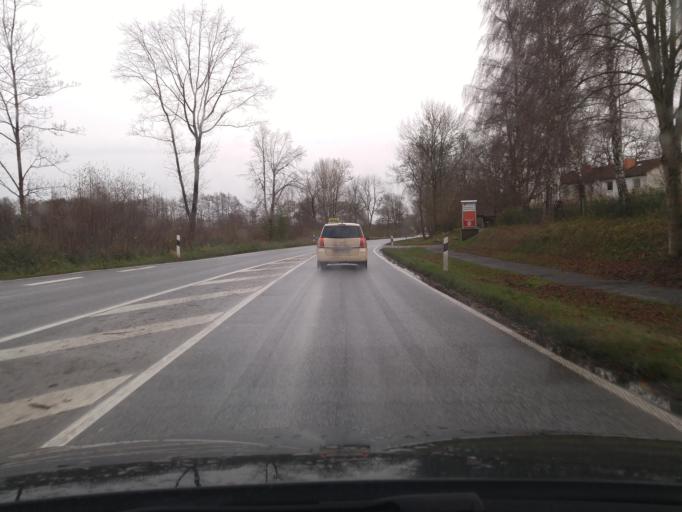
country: DE
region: Schleswig-Holstein
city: Timmendorfer Strand
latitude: 53.9919
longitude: 10.7798
